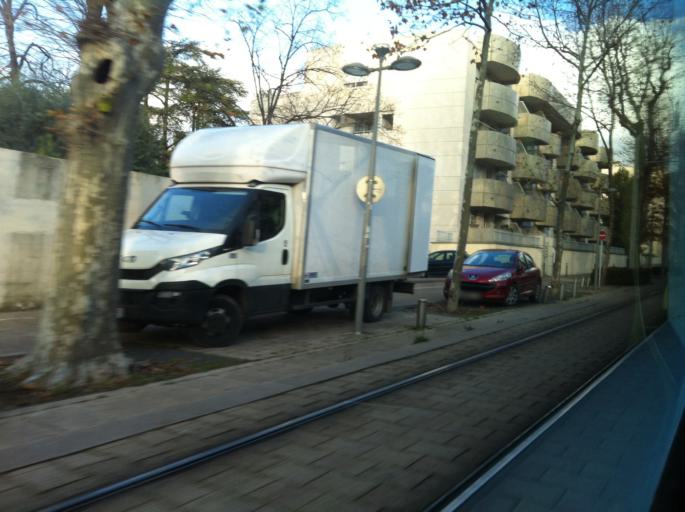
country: FR
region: Languedoc-Roussillon
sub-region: Departement de l'Herault
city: Montpellier
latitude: 43.6248
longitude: 3.8670
